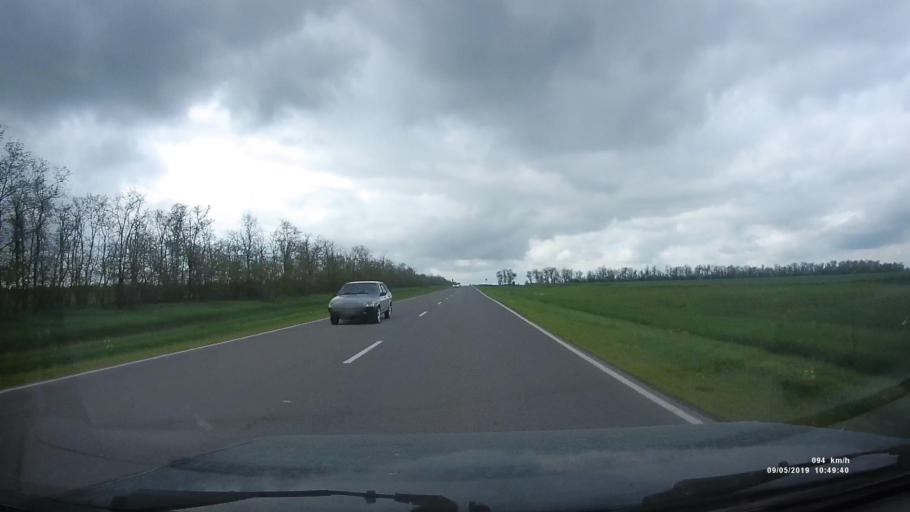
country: RU
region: Rostov
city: Peshkovo
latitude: 46.9391
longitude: 39.3554
